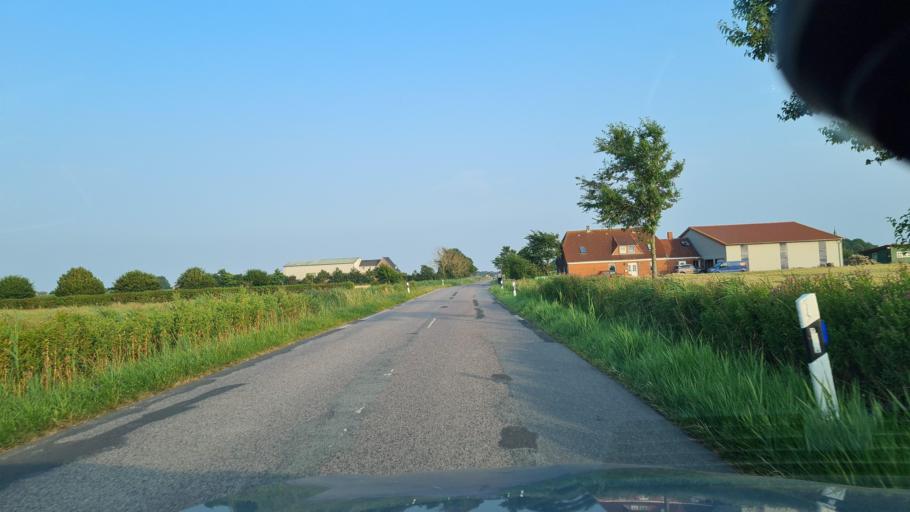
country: DE
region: Schleswig-Holstein
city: Elisabeth-Sophien-Koog
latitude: 54.4974
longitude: 8.8444
